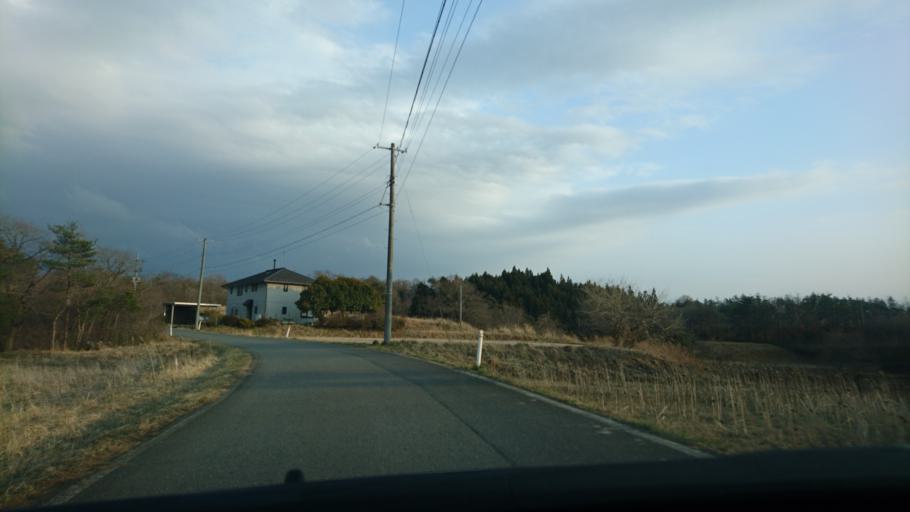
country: JP
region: Iwate
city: Ichinoseki
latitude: 38.8950
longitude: 141.2363
